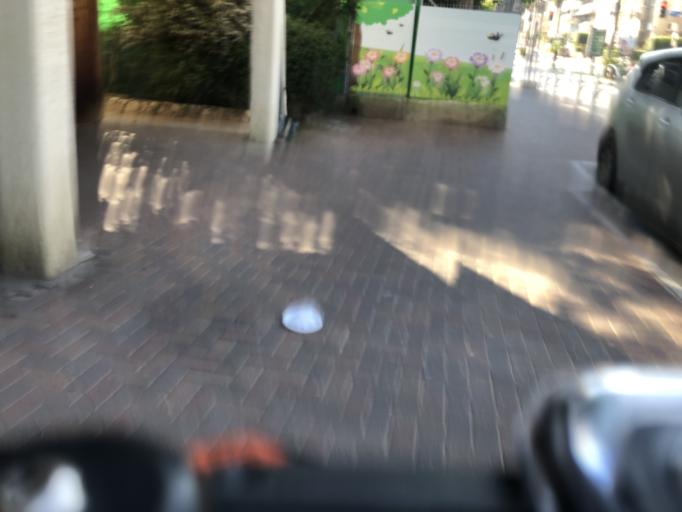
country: IL
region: Tel Aviv
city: Giv`atayim
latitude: 32.0714
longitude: 34.8086
